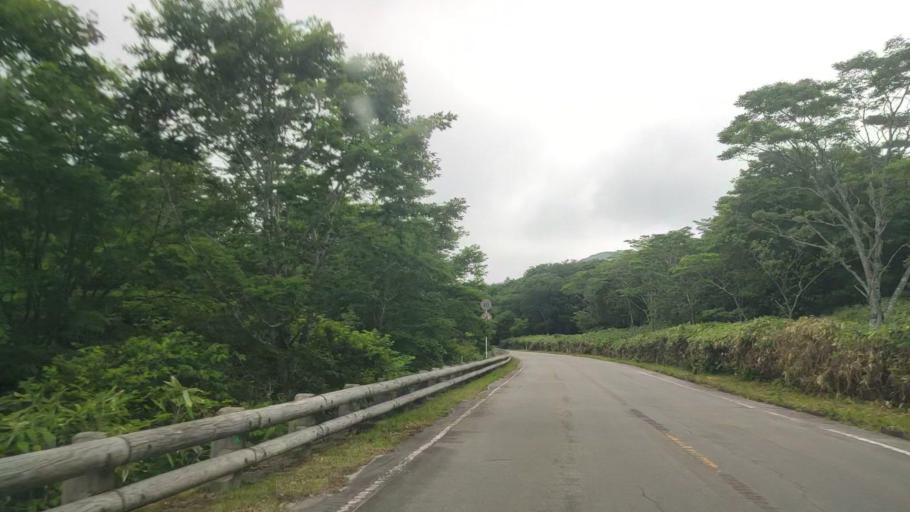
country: JP
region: Tottori
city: Kurayoshi
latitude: 35.3412
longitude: 133.5899
